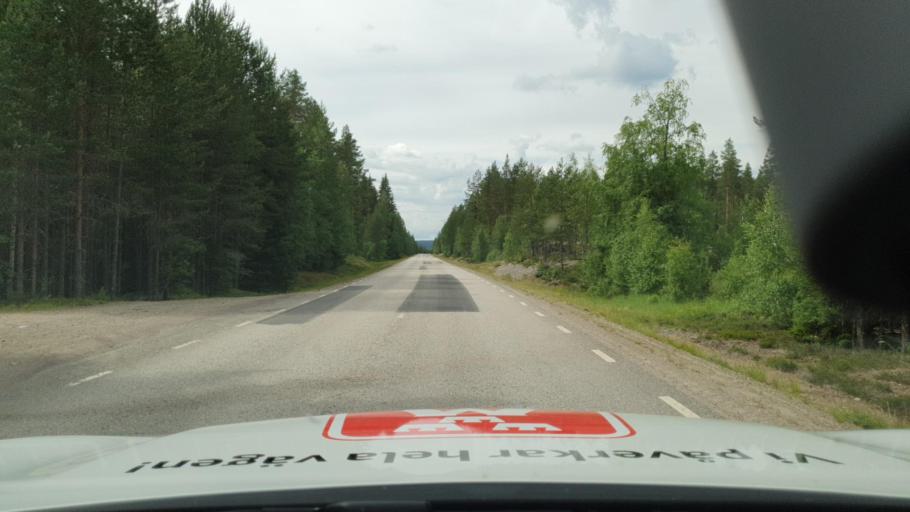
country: NO
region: Hedmark
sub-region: Trysil
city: Innbygda
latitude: 60.9289
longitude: 12.5099
